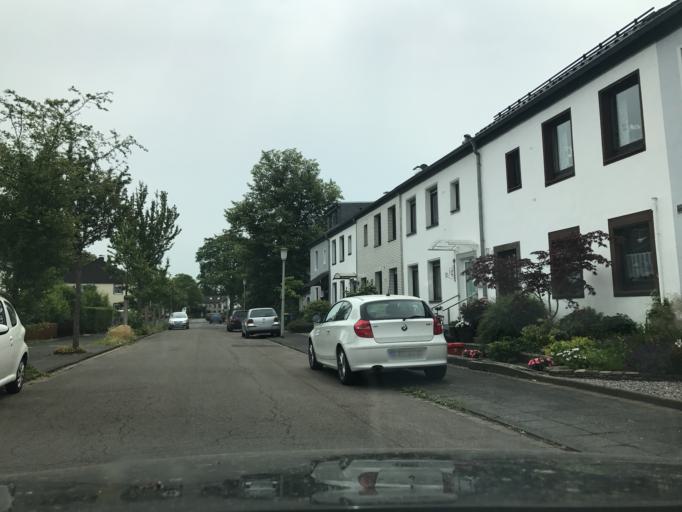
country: DE
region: North Rhine-Westphalia
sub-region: Regierungsbezirk Dusseldorf
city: Krefeld
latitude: 51.3390
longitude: 6.5385
